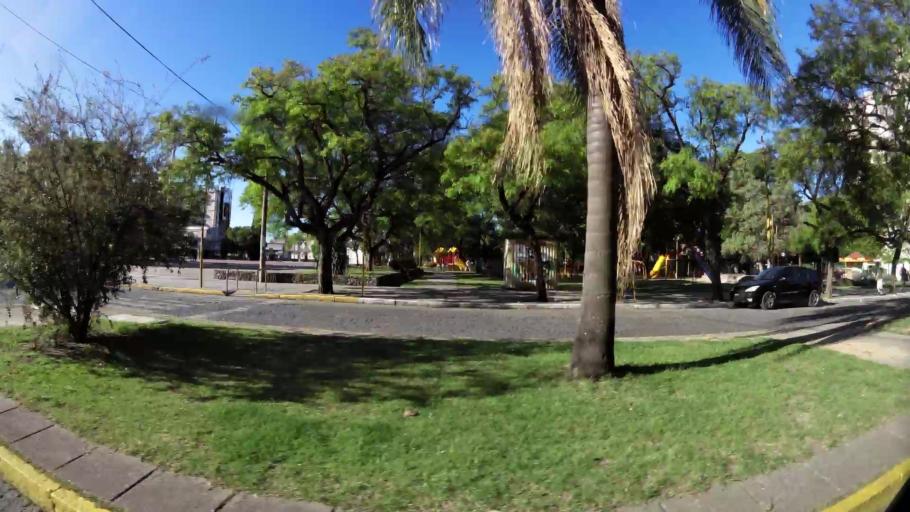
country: AR
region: Cordoba
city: San Francisco
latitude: -31.4310
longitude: -62.0849
